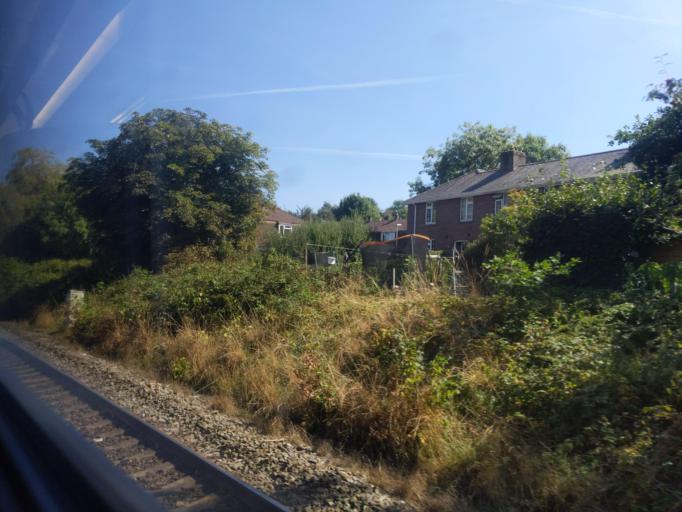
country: GB
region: England
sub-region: Devon
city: Totnes
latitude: 50.4332
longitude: -3.6959
